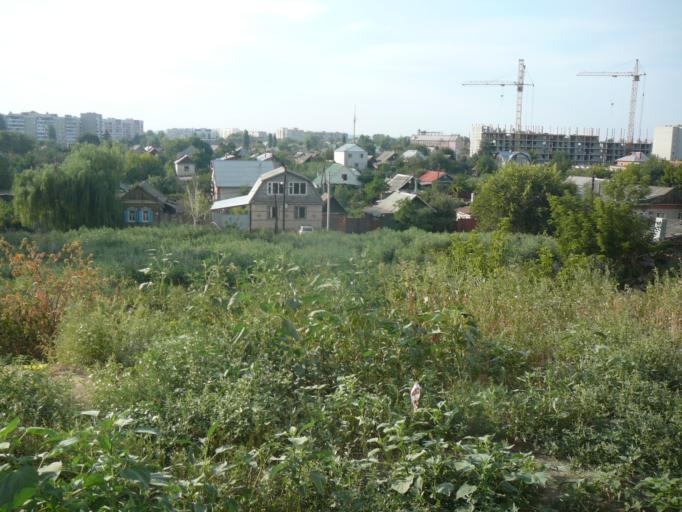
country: RU
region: Saratov
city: Engel's
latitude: 51.4864
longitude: 46.1320
